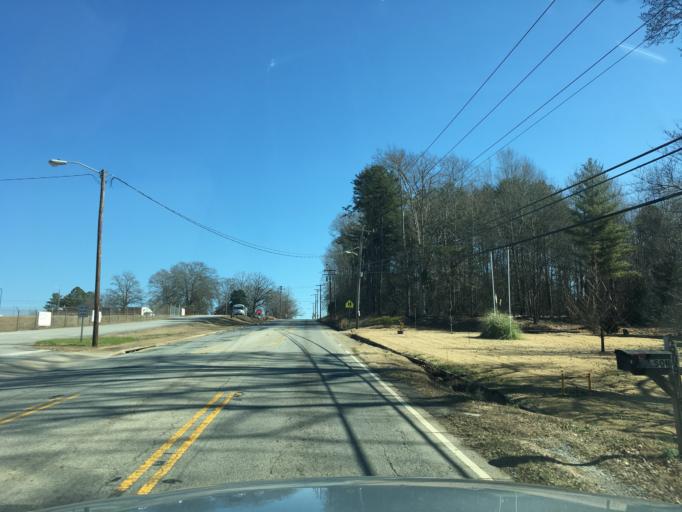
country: US
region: South Carolina
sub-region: Pickens County
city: Liberty
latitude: 34.7863
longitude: -82.7034
